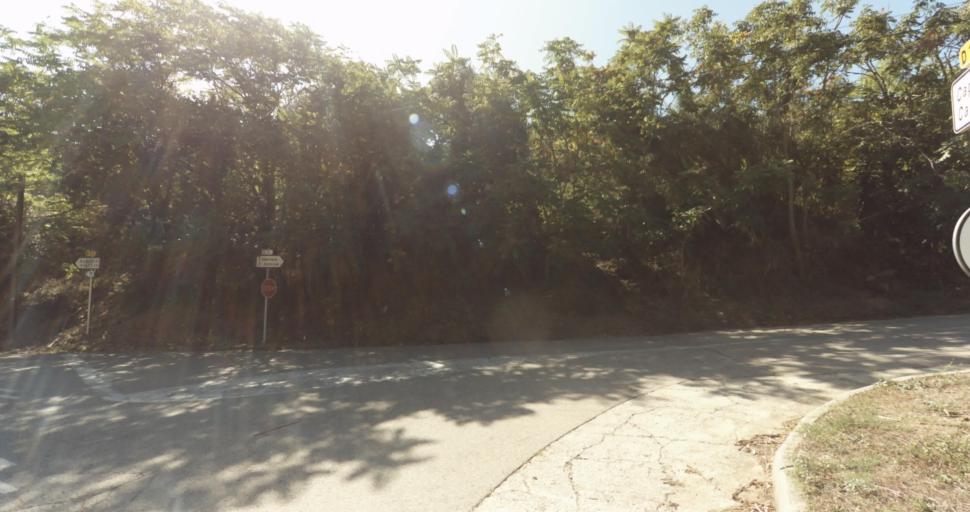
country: FR
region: Corsica
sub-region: Departement de la Corse-du-Sud
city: Ajaccio
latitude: 41.9298
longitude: 8.6945
